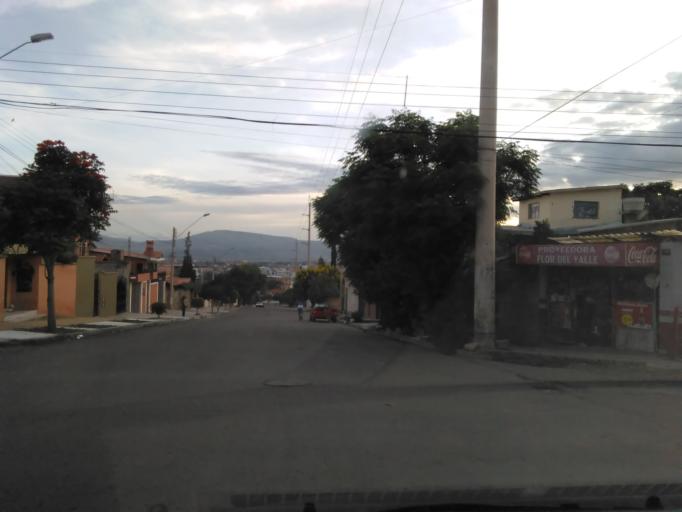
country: BO
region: Cochabamba
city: Cochabamba
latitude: -17.3631
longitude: -66.1601
